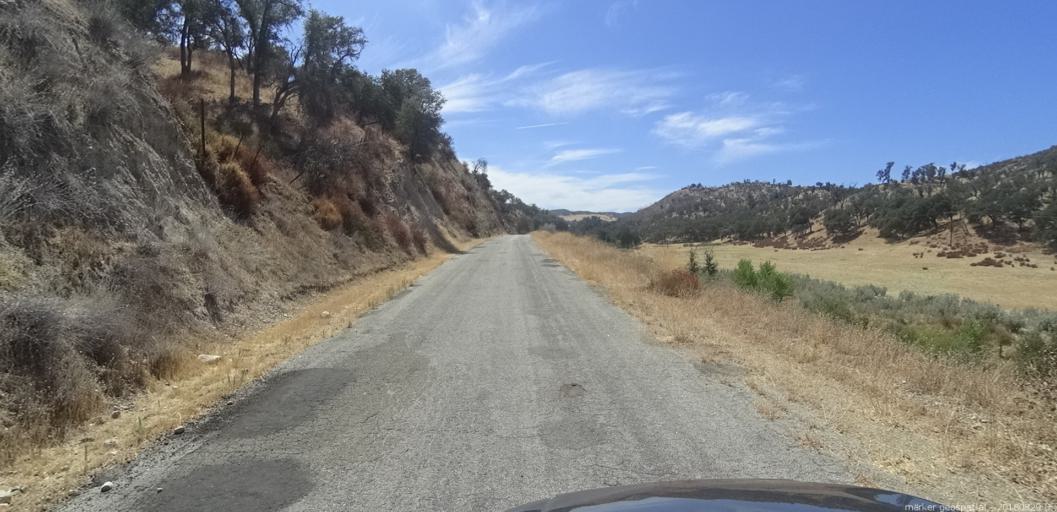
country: US
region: California
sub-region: San Luis Obispo County
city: Lake Nacimiento
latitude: 35.8558
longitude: -121.0356
